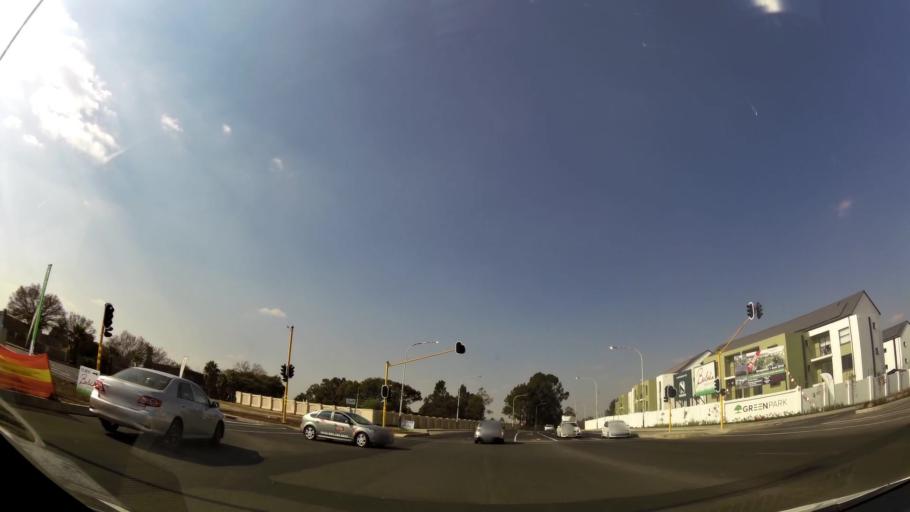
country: ZA
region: Gauteng
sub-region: Ekurhuleni Metropolitan Municipality
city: Boksburg
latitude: -26.1926
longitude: 28.2295
